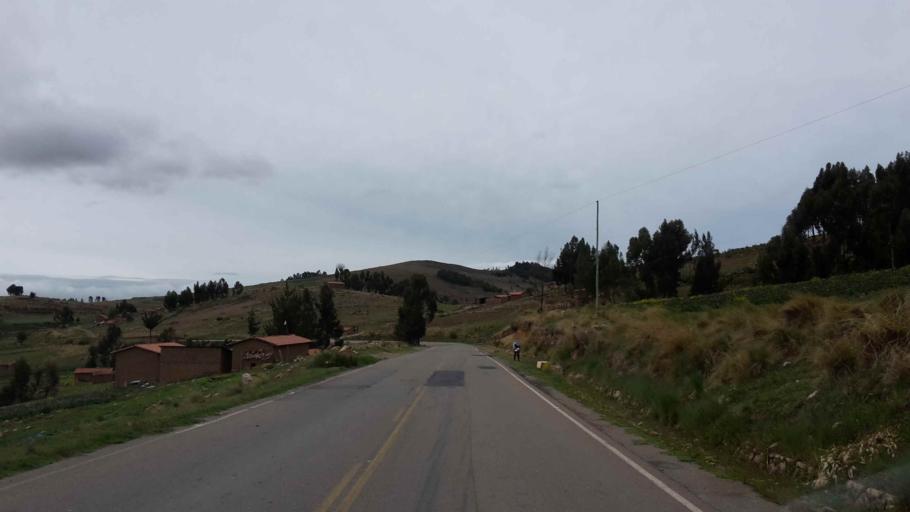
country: BO
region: Cochabamba
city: Arani
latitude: -17.4698
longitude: -65.6532
